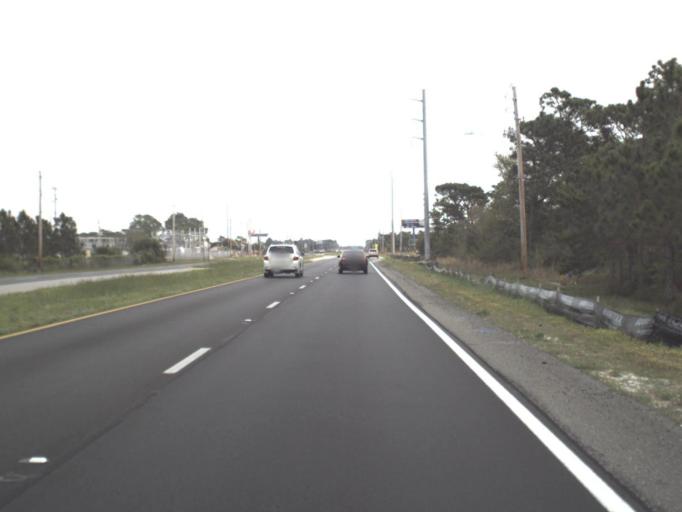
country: US
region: Florida
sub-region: Santa Rosa County
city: Woodlawn Beach
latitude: 30.4006
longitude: -86.9939
